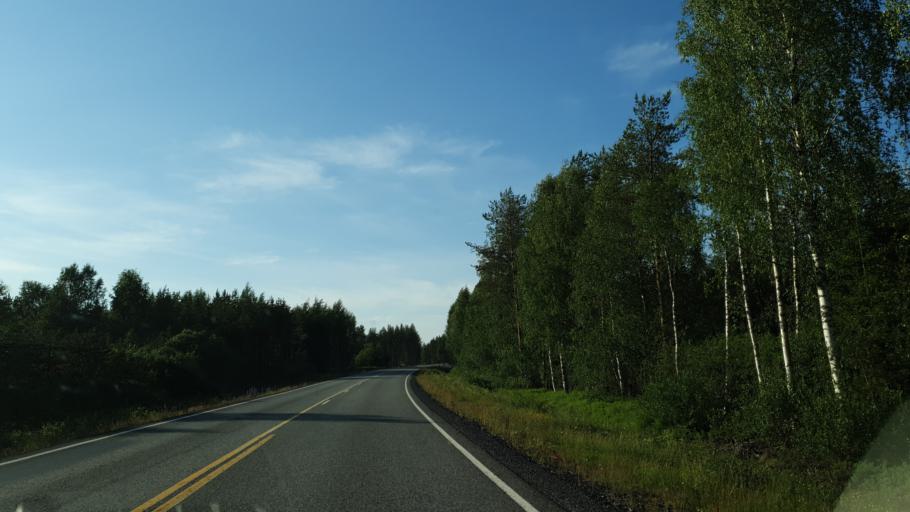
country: FI
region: Kainuu
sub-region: Kehys-Kainuu
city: Kuhmo
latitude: 64.0787
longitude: 29.4871
